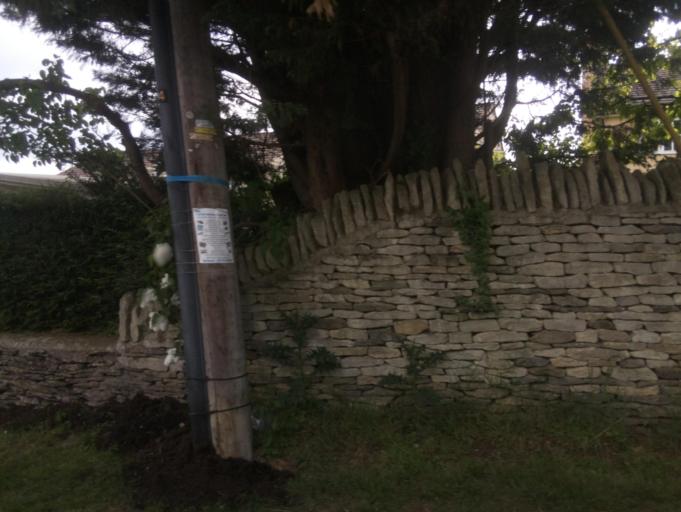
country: GB
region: England
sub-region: Wiltshire
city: Luckington
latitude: 51.5756
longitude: -2.2144
